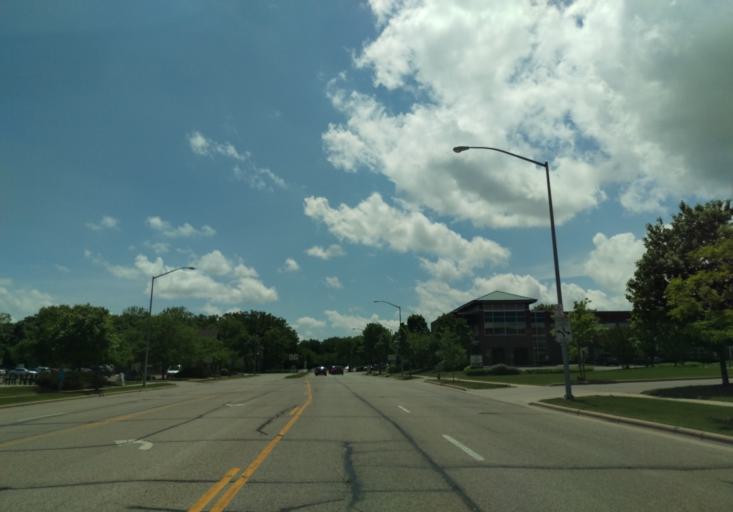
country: US
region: Wisconsin
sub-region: Dane County
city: Middleton
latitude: 43.0764
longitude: -89.5188
